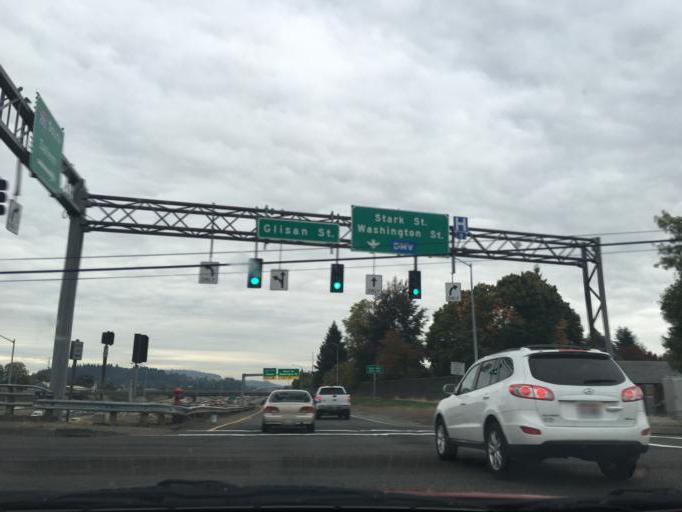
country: US
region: Oregon
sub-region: Multnomah County
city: Lents
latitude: 45.5264
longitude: -122.5660
